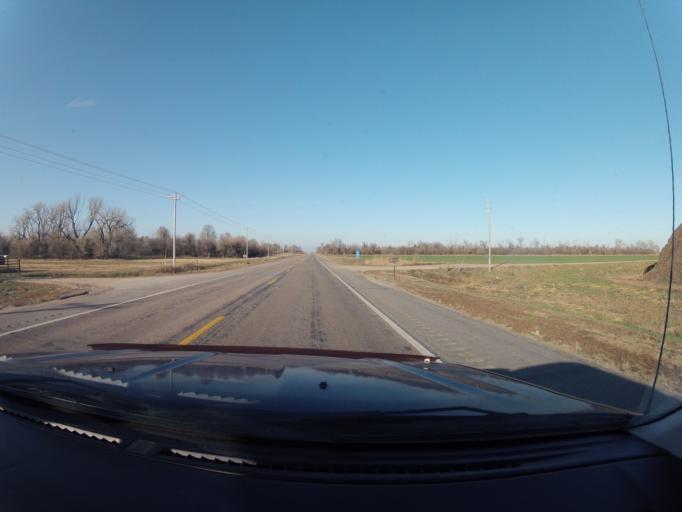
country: US
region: Nebraska
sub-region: Kearney County
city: Minden
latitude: 40.6046
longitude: -98.9516
